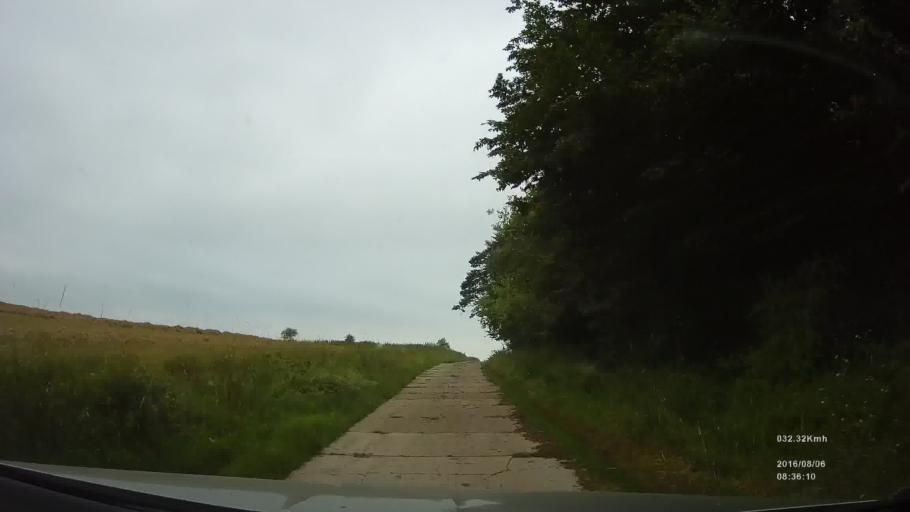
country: SK
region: Presovsky
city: Svidnik
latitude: 49.3435
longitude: 21.5834
